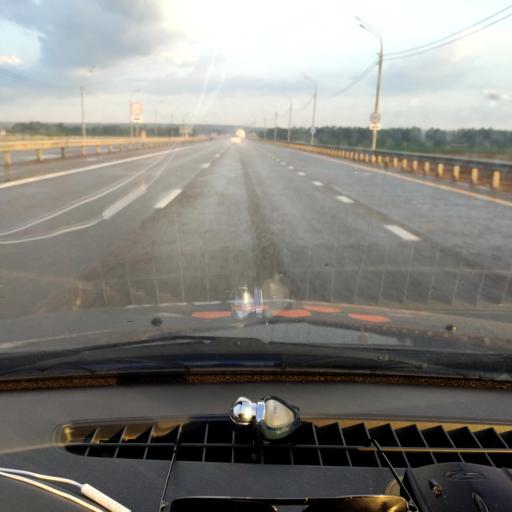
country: RU
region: Lipetsk
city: Zadonsk
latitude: 52.3710
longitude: 38.9125
